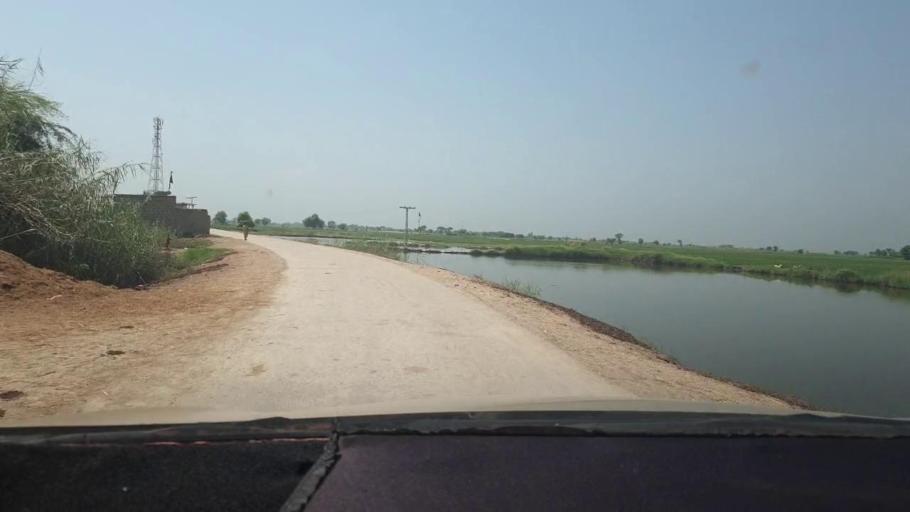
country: PK
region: Sindh
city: Miro Khan
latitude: 27.6616
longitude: 68.0817
